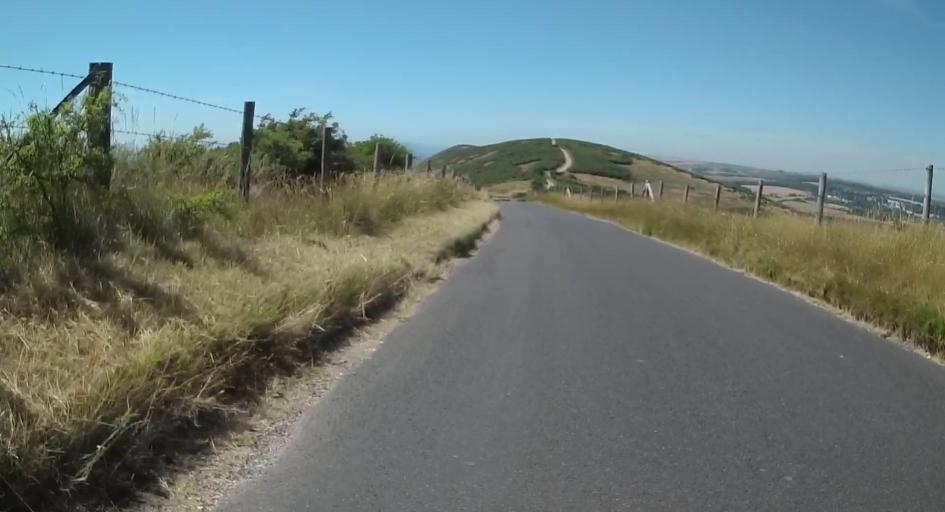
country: GB
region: England
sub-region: Dorset
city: Wool
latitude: 50.6294
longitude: -2.1650
